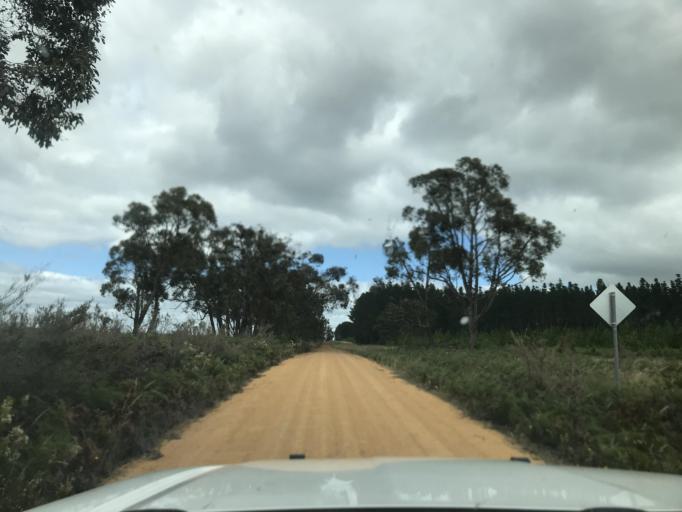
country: AU
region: South Australia
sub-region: Wattle Range
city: Penola
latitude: -37.3171
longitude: 141.1577
